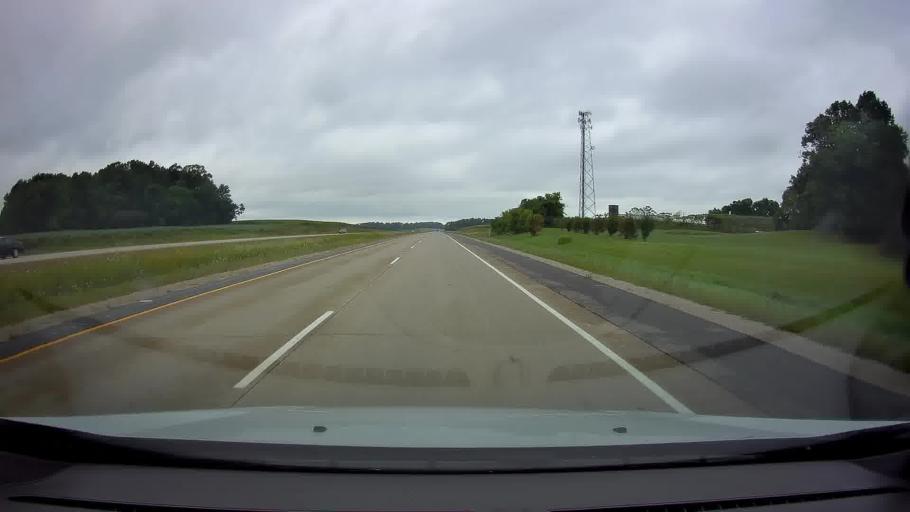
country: US
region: Wisconsin
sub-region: Brown County
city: Pulaski
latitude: 44.6461
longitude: -88.2922
